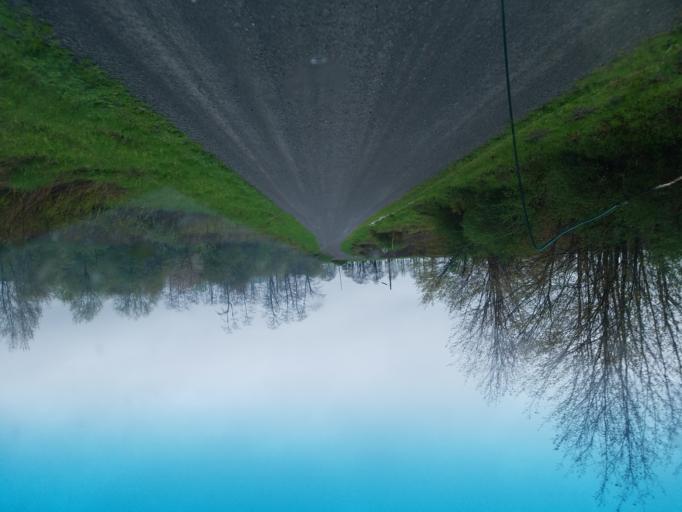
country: US
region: New York
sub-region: Allegany County
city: Andover
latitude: 41.9892
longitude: -77.7221
